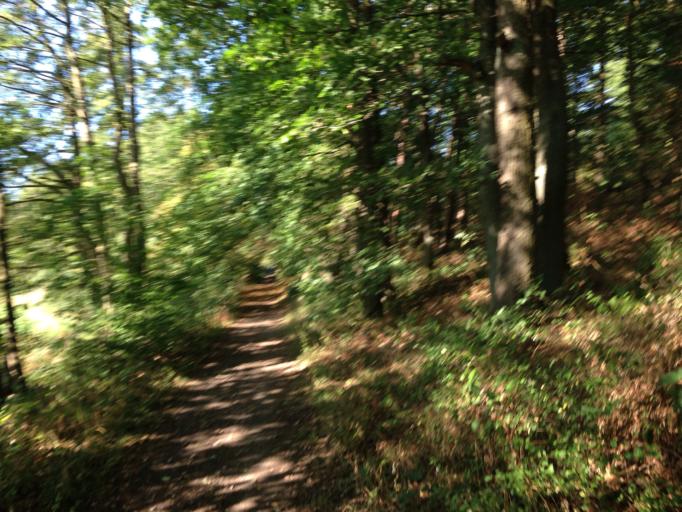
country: DE
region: Hesse
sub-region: Regierungsbezirk Giessen
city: Heuchelheim
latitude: 50.6300
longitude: 8.6502
